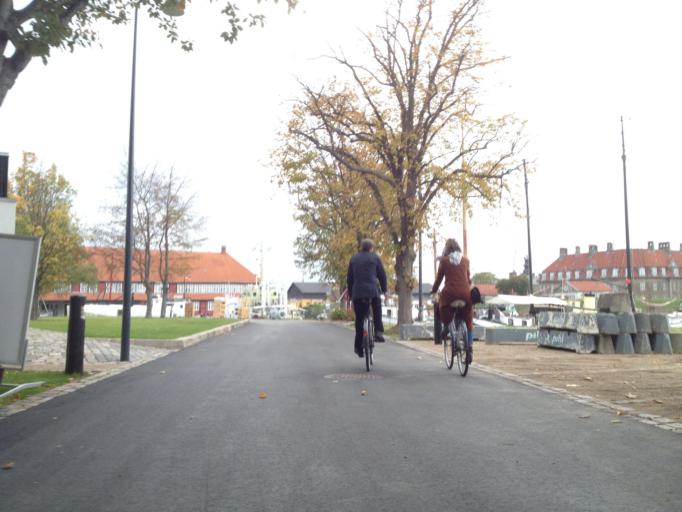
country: DK
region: Capital Region
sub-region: Kobenhavn
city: Christianshavn
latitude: 55.6874
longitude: 12.6099
